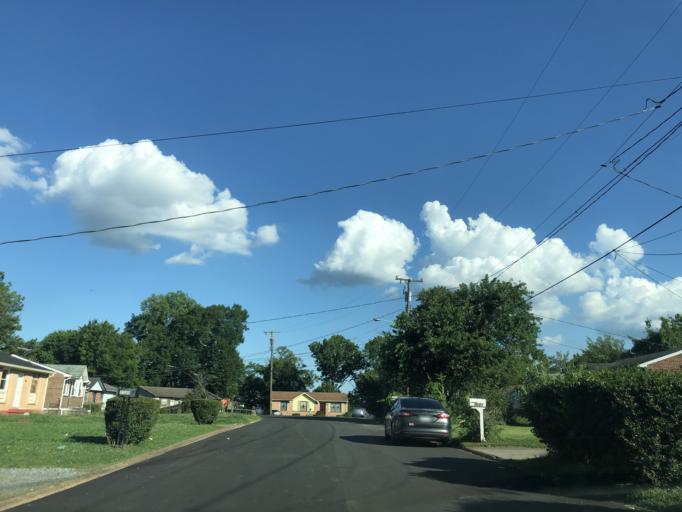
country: US
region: Tennessee
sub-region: Davidson County
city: Nashville
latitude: 36.1851
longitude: -86.8459
